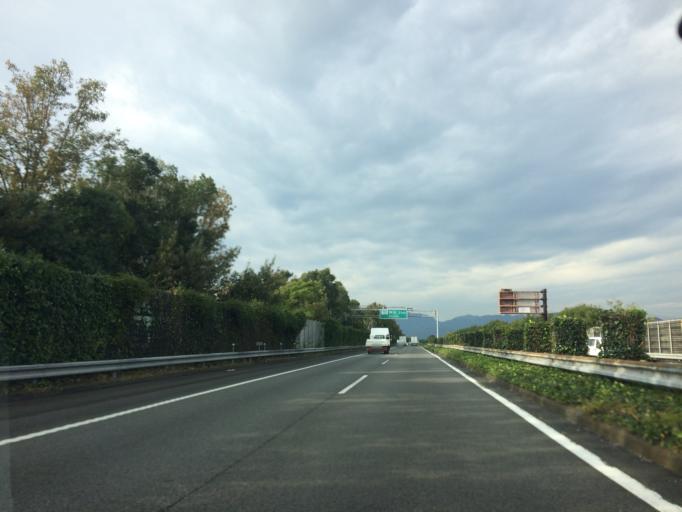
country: JP
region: Shizuoka
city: Shizuoka-shi
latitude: 34.9582
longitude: 138.4170
